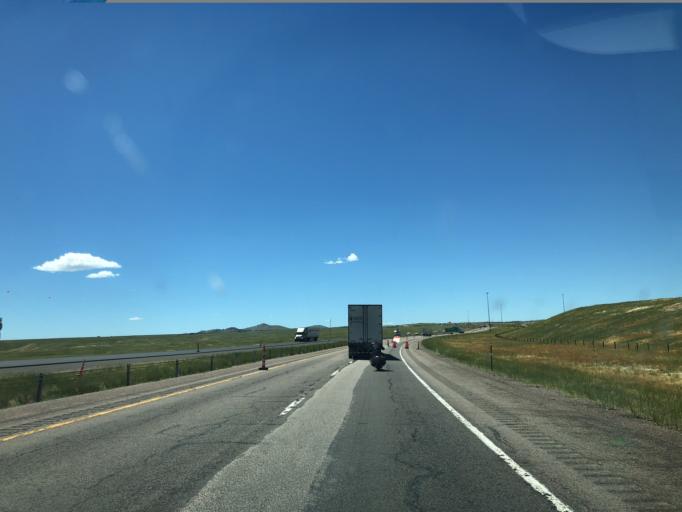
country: US
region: Wyoming
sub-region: Laramie County
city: Cheyenne
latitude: 41.0974
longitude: -105.1048
